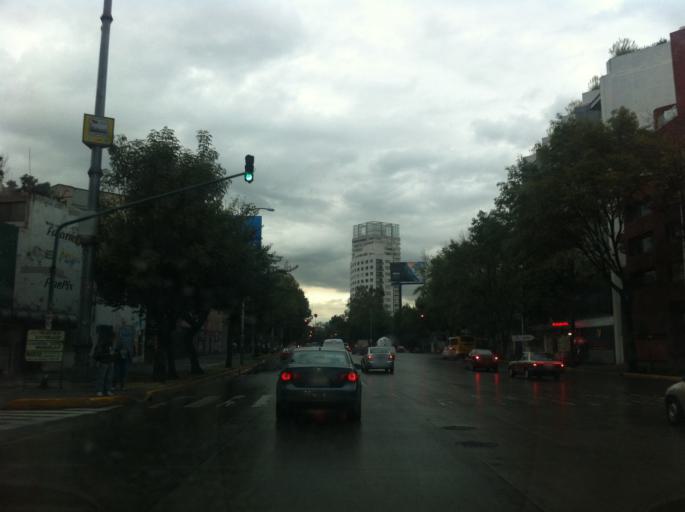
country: MX
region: Mexico City
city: Benito Juarez
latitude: 19.4069
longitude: -99.1787
